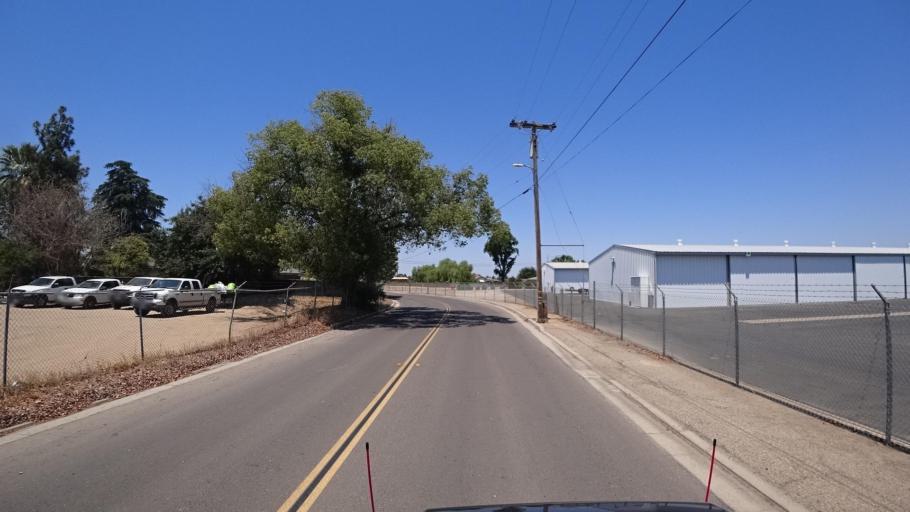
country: US
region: California
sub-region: Fresno County
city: West Park
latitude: 36.7325
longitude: -119.8256
